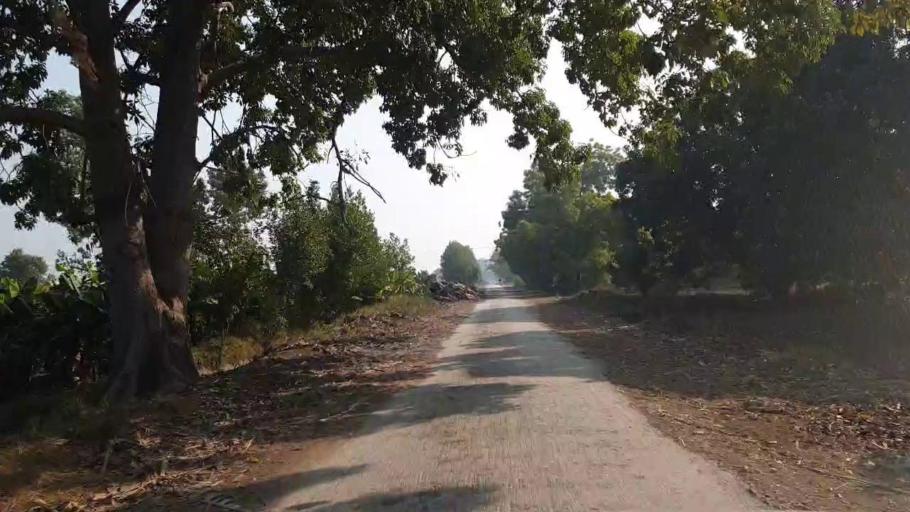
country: PK
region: Sindh
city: Sakrand
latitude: 25.9918
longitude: 68.3676
